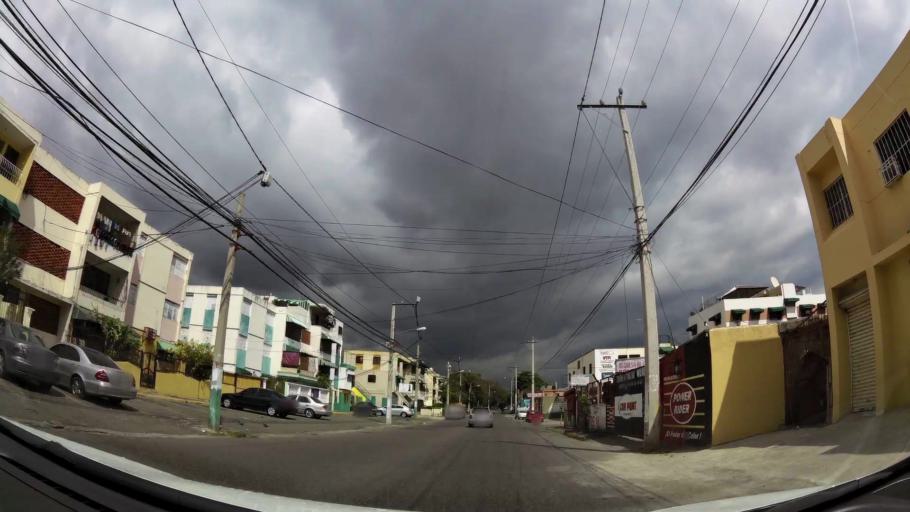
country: DO
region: Nacional
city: La Agustina
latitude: 18.4935
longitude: -69.9276
